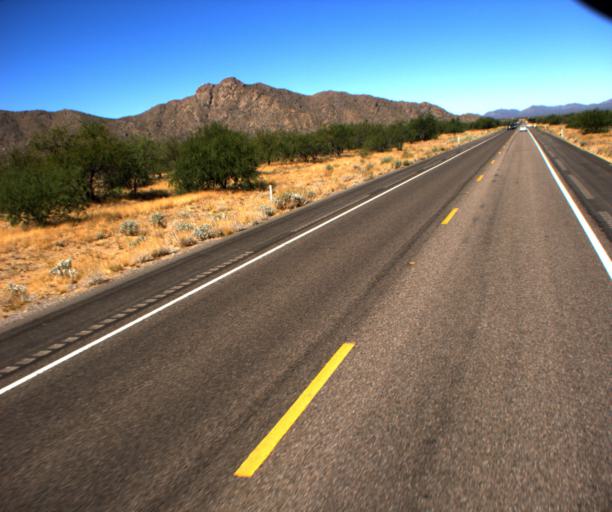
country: US
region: Arizona
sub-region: Pima County
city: Sells
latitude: 32.0141
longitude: -111.6423
